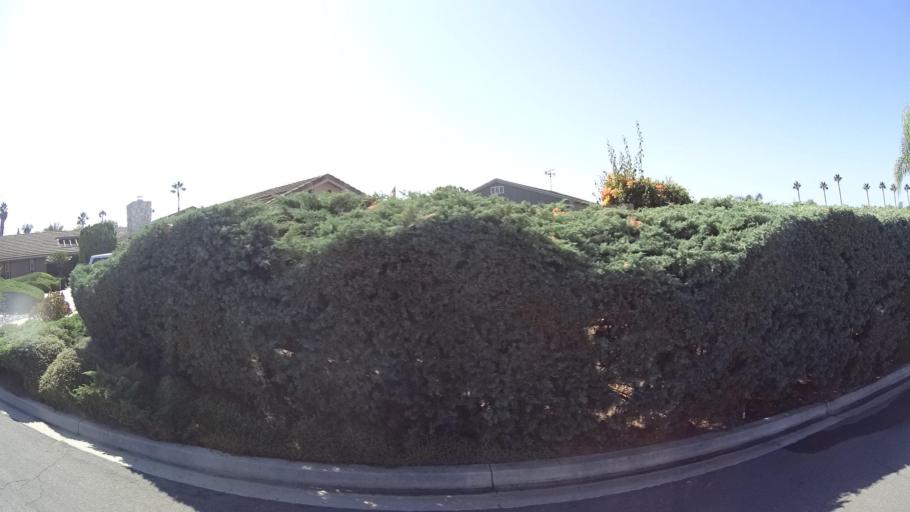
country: US
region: California
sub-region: San Diego County
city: Granite Hills
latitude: 32.7907
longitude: -116.8967
